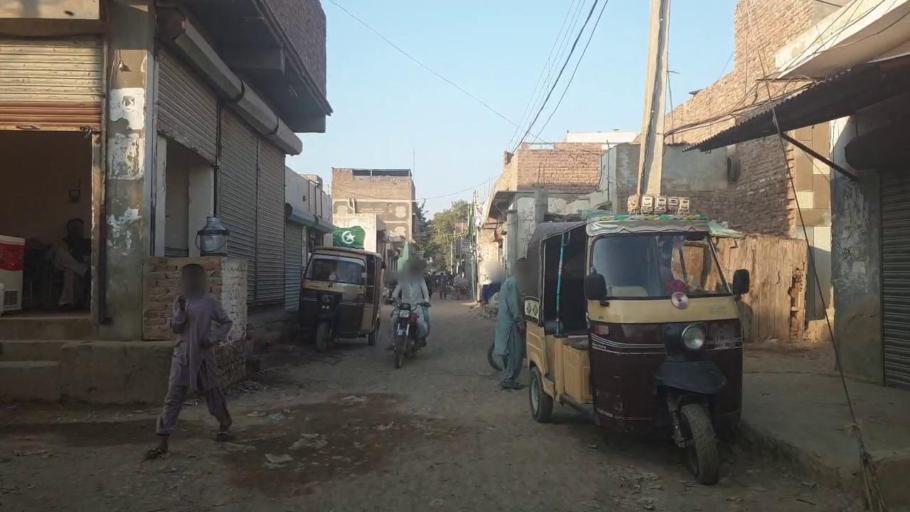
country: PK
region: Sindh
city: Jamshoro
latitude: 25.4447
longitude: 68.2960
